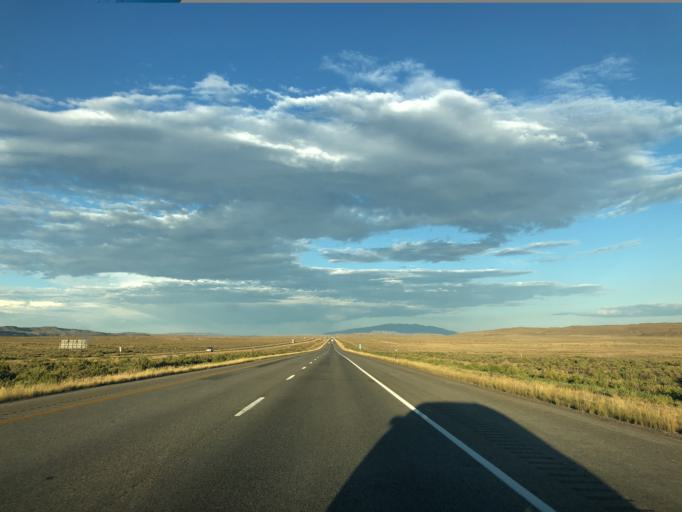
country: US
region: Wyoming
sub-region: Carbon County
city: Rawlins
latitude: 41.7687
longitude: -107.0455
